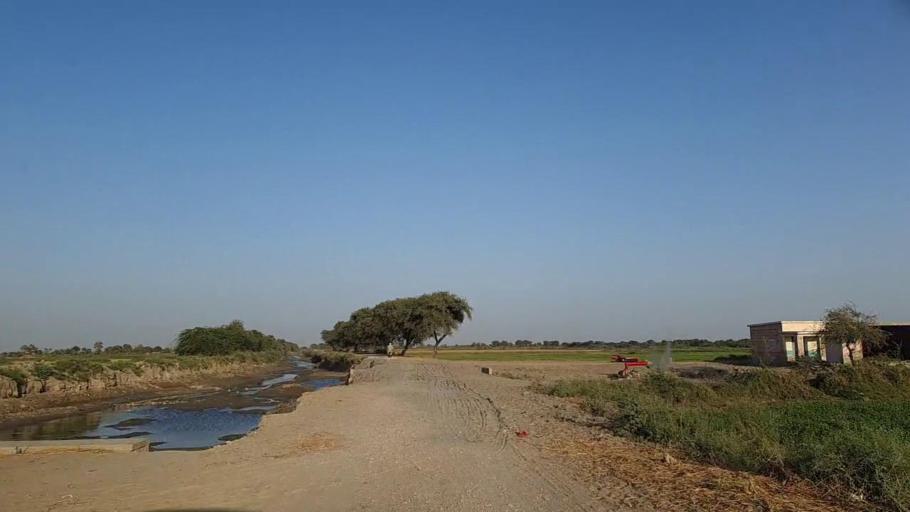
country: PK
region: Sindh
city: Jati
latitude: 24.4141
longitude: 68.3157
